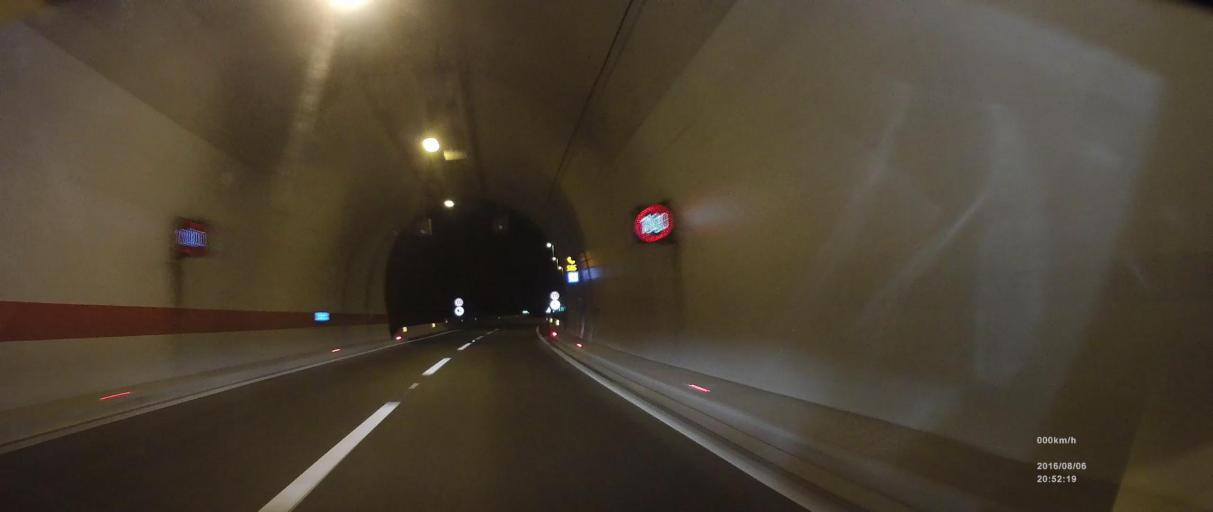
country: BA
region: Federation of Bosnia and Herzegovina
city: Ljubuski
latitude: 43.1275
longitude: 17.4847
